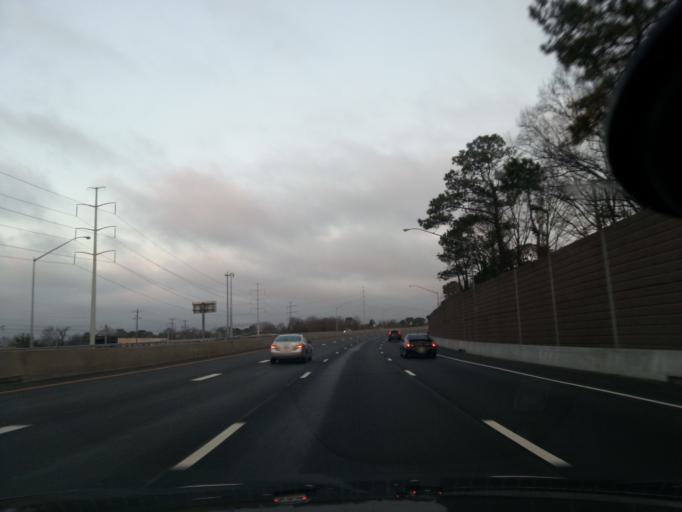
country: US
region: Virginia
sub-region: City of Chesapeake
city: Chesapeake
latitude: 36.8443
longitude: -76.2388
